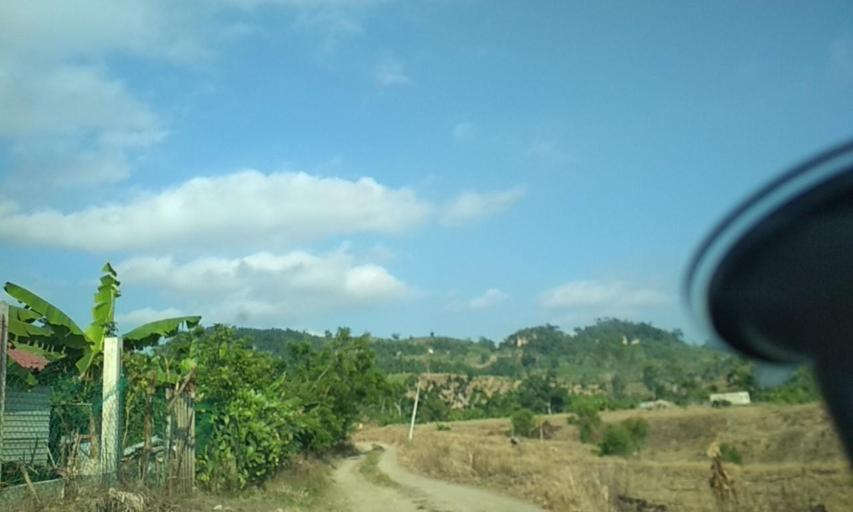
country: MX
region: Veracruz
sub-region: Papantla
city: Polutla
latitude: 20.6001
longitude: -97.2582
